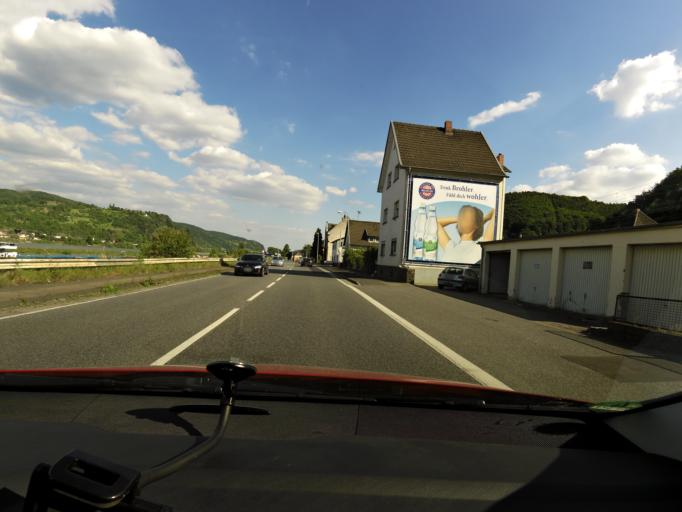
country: DE
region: Rheinland-Pfalz
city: Brohl-Lutzing
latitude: 50.4918
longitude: 7.3201
